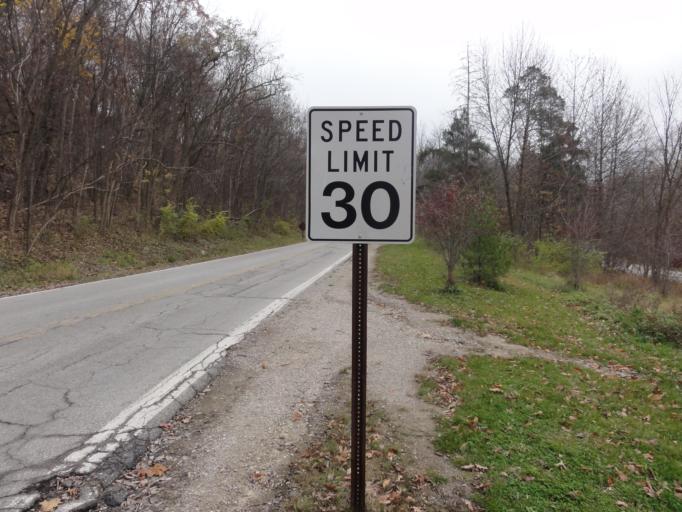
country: US
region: Ohio
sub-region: Cuyahoga County
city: Rocky River
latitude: 41.4660
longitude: -81.8278
